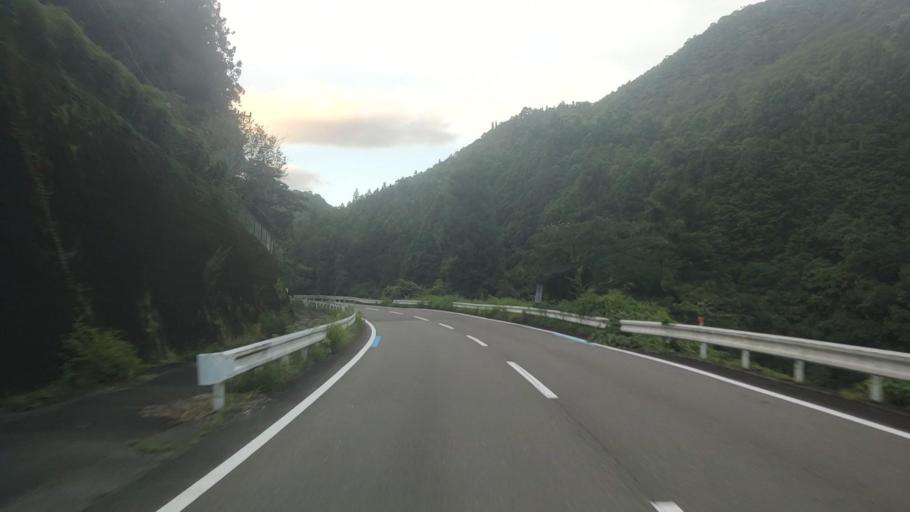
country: JP
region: Wakayama
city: Shingu
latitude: 33.8065
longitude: 135.7346
